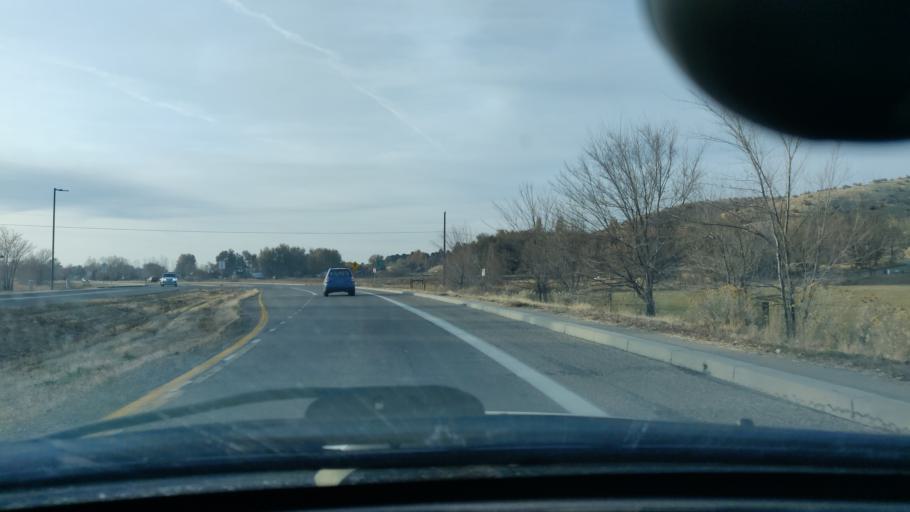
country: US
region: Idaho
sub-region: Ada County
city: Eagle
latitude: 43.6860
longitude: -116.2930
